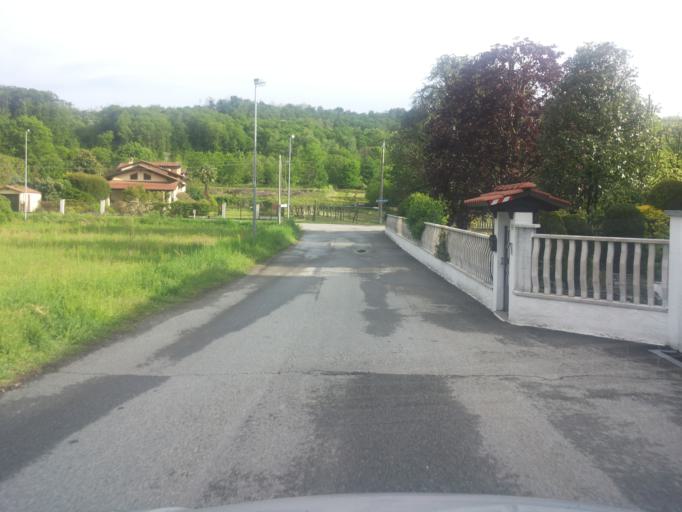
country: IT
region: Piedmont
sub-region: Provincia di Torino
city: Cossano Canavese
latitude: 45.3861
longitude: 7.9933
